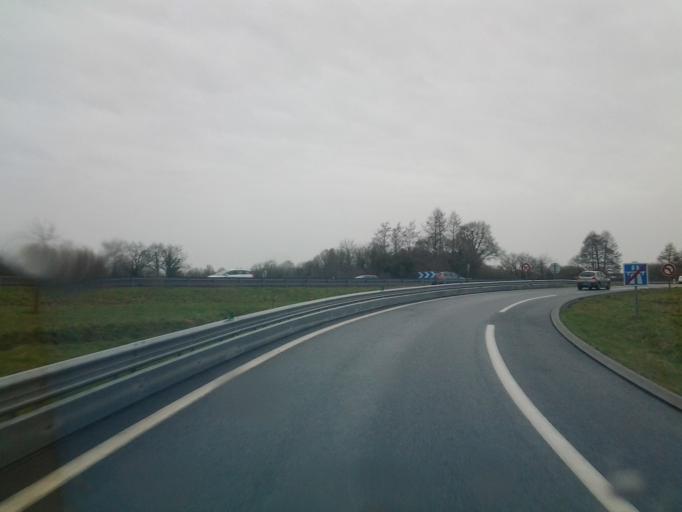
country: FR
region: Pays de la Loire
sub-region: Departement de la Vendee
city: Les Clouzeaux
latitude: 46.6447
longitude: -1.5169
